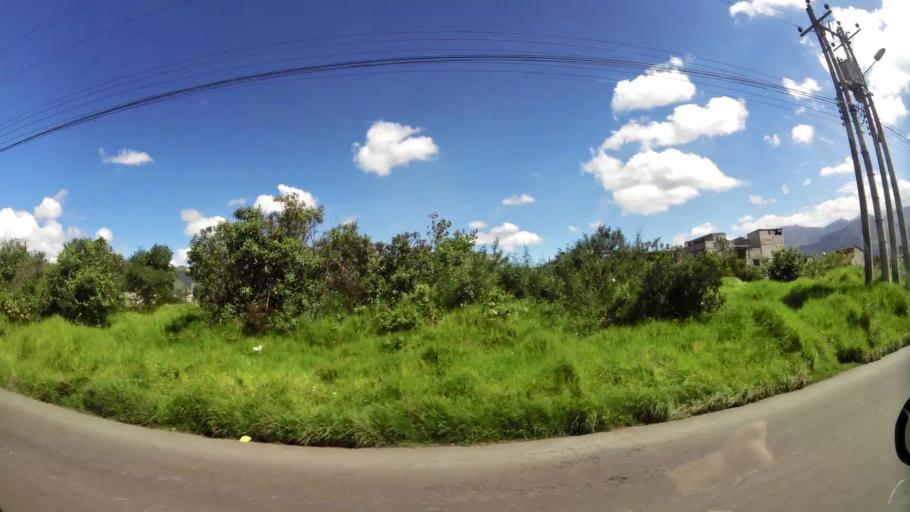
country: EC
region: Pichincha
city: Quito
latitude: -0.2940
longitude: -78.5428
